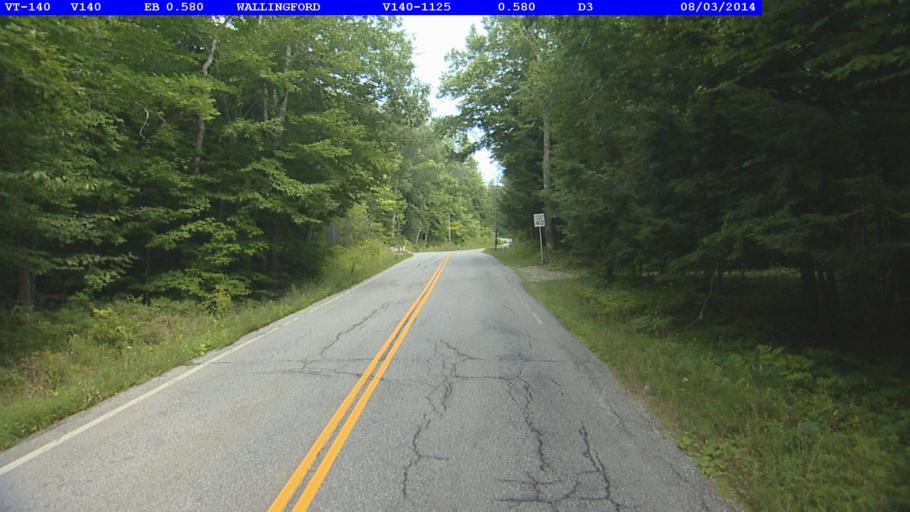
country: US
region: Vermont
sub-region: Rutland County
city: Rutland
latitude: 43.4682
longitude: -72.9672
